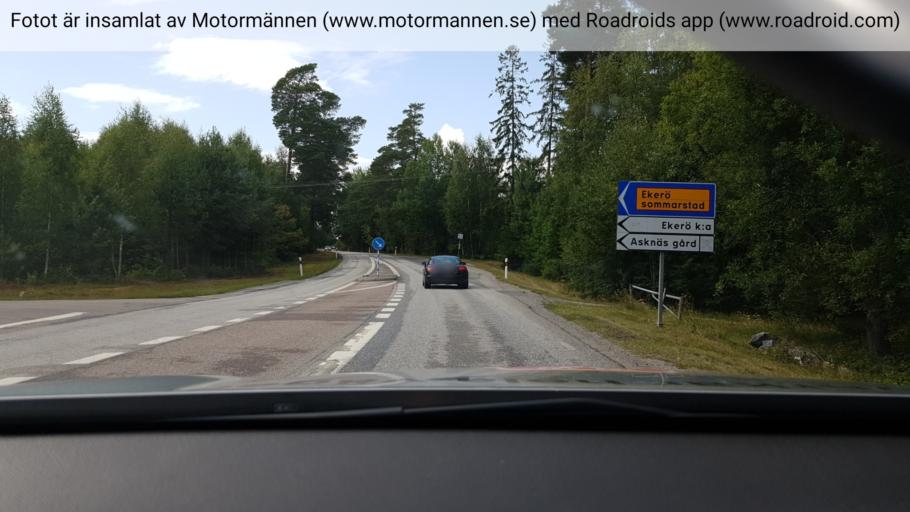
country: SE
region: Stockholm
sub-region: Ekero Kommun
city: Ekeroe
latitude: 59.2821
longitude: 17.7477
